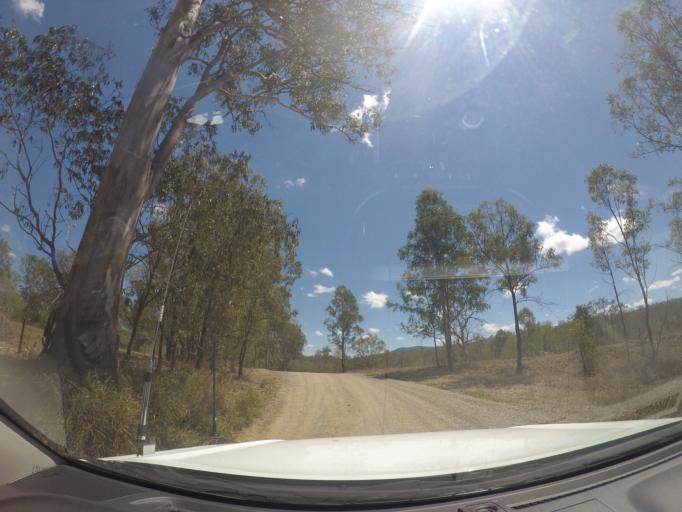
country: AU
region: Queensland
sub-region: Logan
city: North Maclean
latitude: -27.8324
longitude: 152.8674
